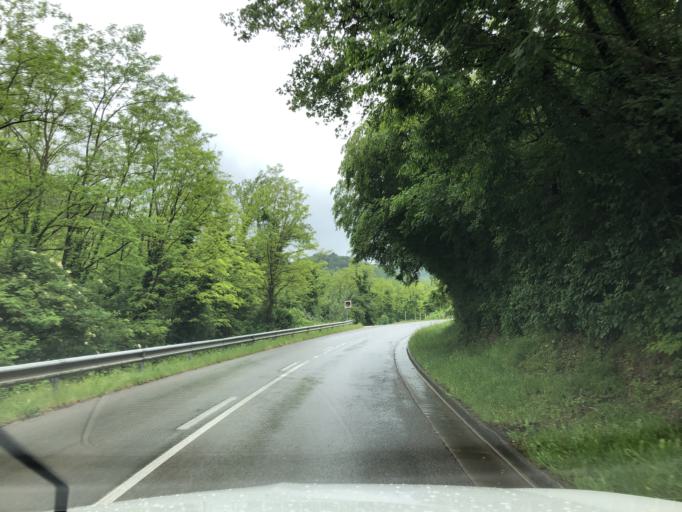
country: SI
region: Koper-Capodistria
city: Prade
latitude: 45.5141
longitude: 13.7800
